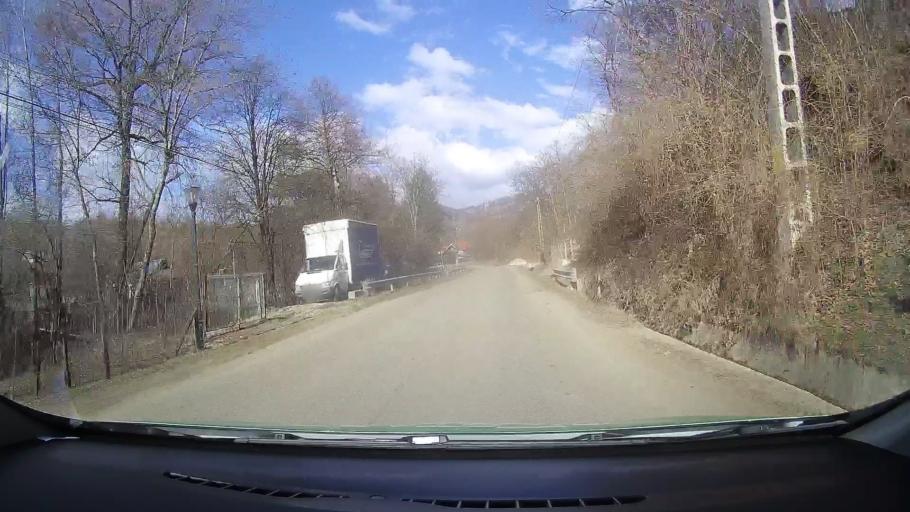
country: RO
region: Dambovita
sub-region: Comuna Varfuri
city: Varfuri
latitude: 45.0875
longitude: 25.4970
